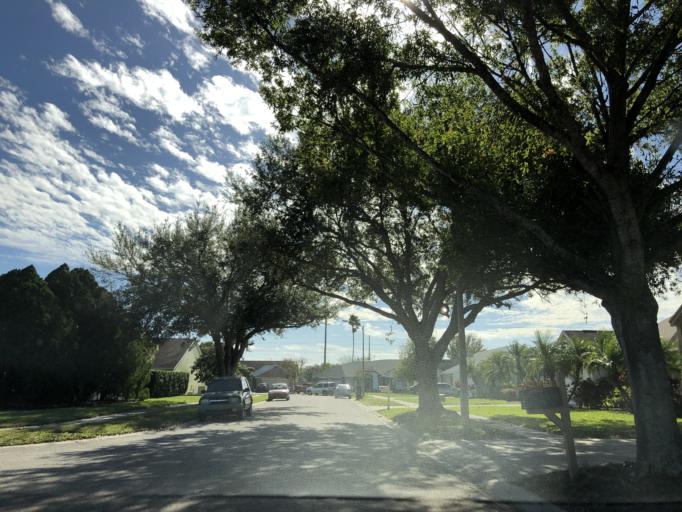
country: US
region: Florida
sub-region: Orange County
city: Hunters Creek
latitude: 28.3776
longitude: -81.4082
